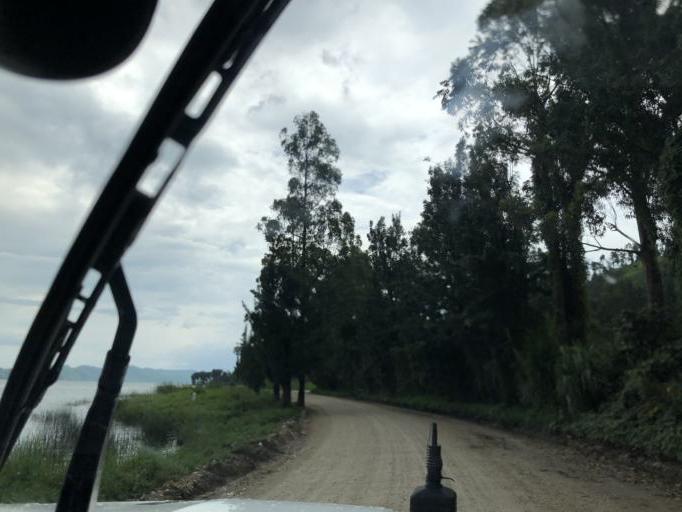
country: CD
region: Nord Kivu
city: Sake
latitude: -1.5994
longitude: 29.0376
